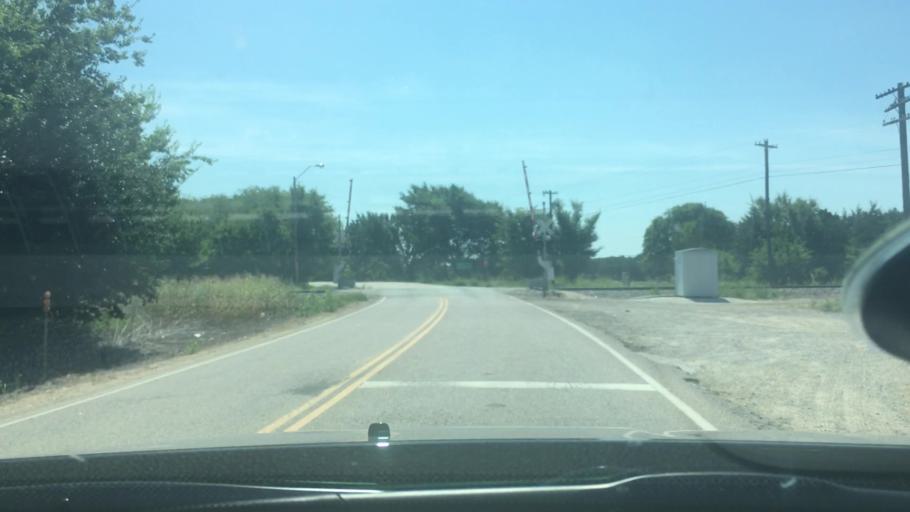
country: US
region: Oklahoma
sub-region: Bryan County
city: Colbert
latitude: 33.8535
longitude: -96.5004
